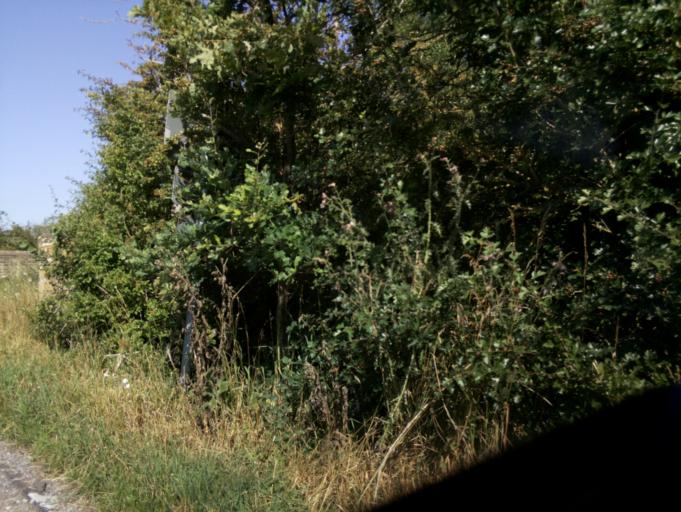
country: GB
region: England
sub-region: Oxfordshire
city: Bampton
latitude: 51.7057
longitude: -1.5197
